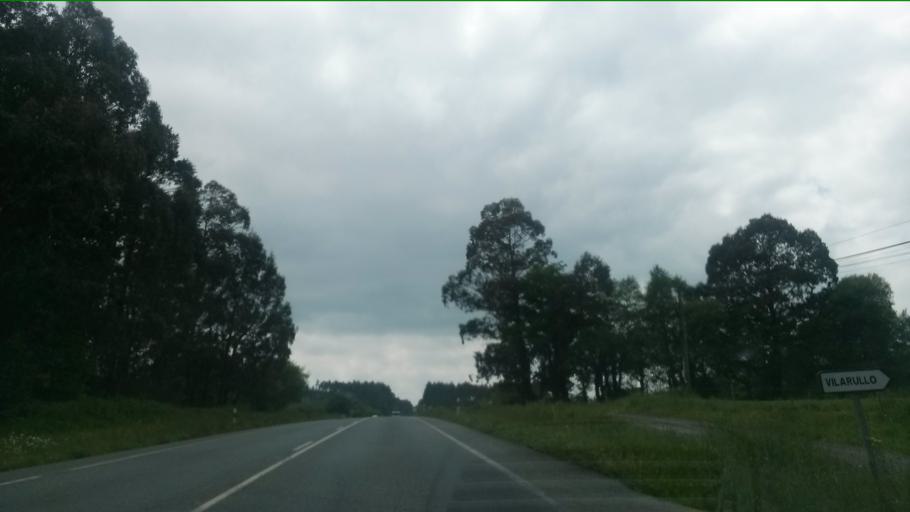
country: ES
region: Galicia
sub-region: Provincia da Coruna
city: Curtis
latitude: 43.1268
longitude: -8.0577
